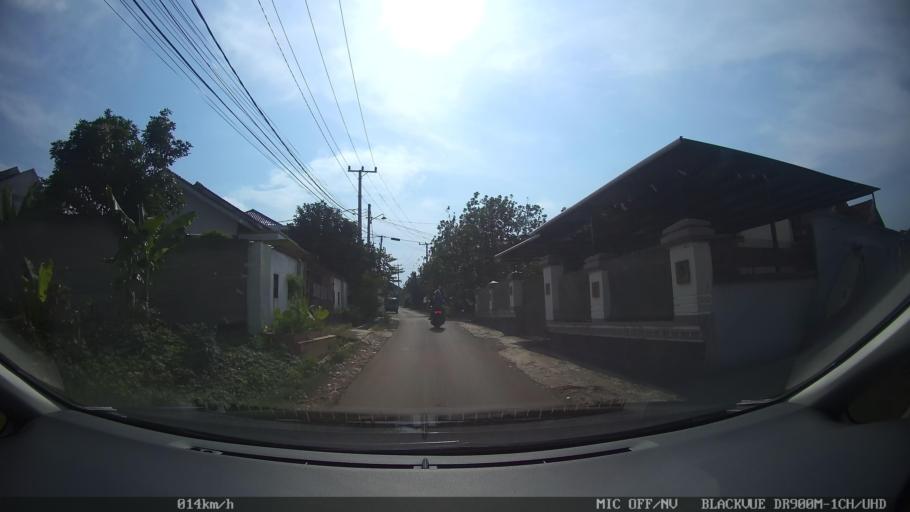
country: ID
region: Lampung
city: Kedaton
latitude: -5.3856
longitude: 105.2354
